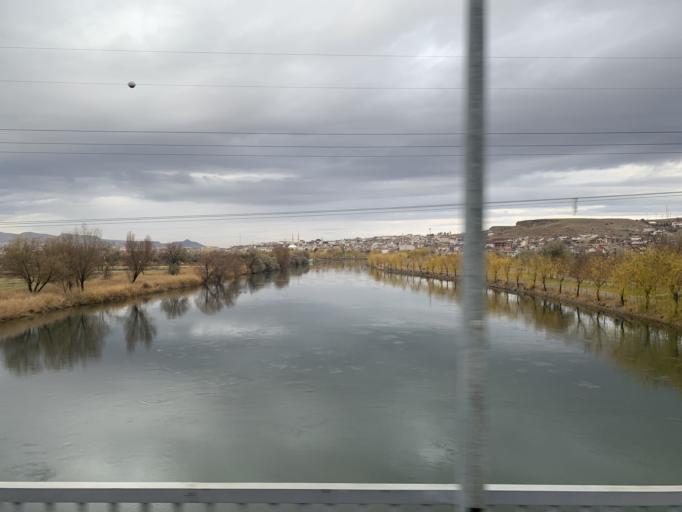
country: TR
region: Nevsehir
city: Avanos
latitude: 38.7163
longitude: 34.8596
